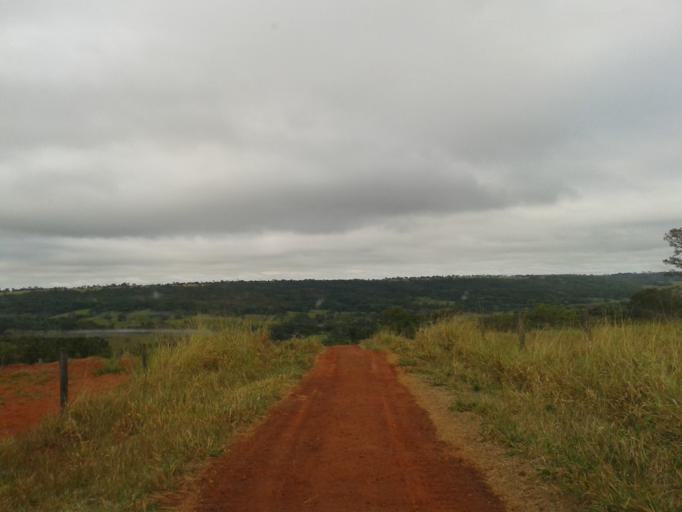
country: BR
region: Minas Gerais
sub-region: Campina Verde
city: Campina Verde
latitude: -19.4226
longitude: -49.6460
